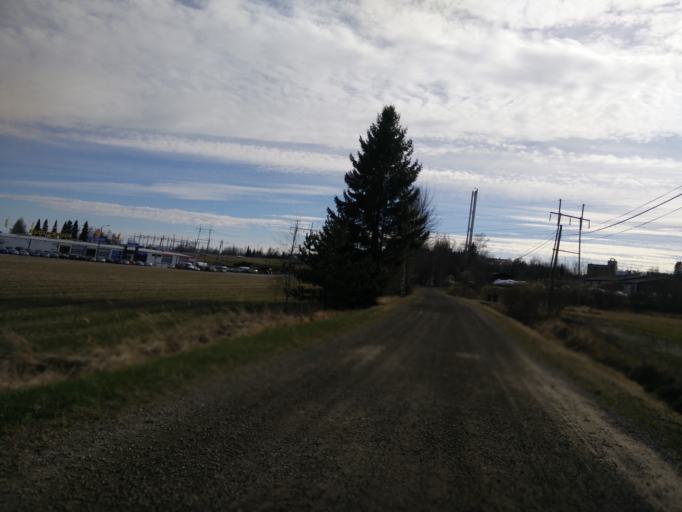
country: FI
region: Pirkanmaa
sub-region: Tampere
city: Orivesi
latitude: 61.6887
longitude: 24.3726
